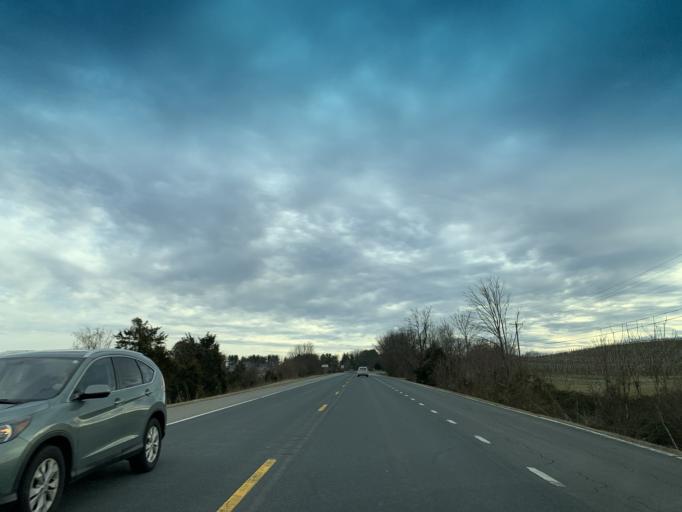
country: US
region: Maryland
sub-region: Washington County
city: Keedysville
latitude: 39.4277
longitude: -77.6612
